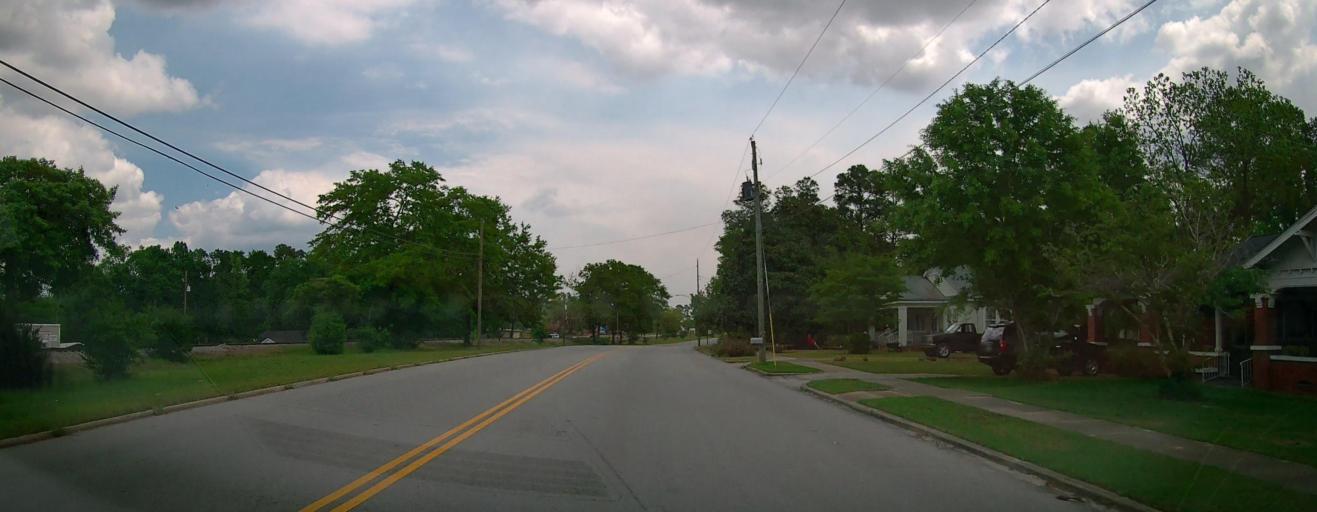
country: US
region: Georgia
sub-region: Treutlen County
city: Soperton
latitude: 32.3765
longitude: -82.5906
